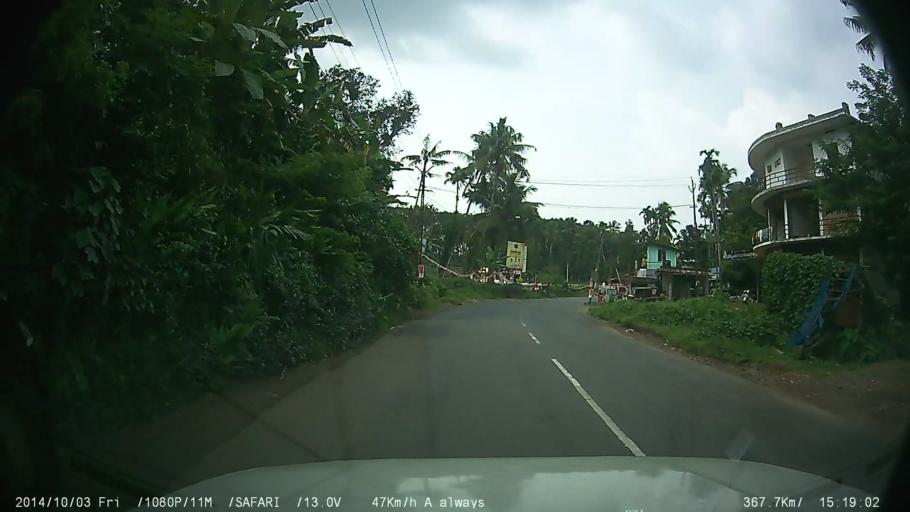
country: IN
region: Kerala
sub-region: Ernakulam
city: Muvattupuzha
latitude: 9.8994
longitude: 76.5876
